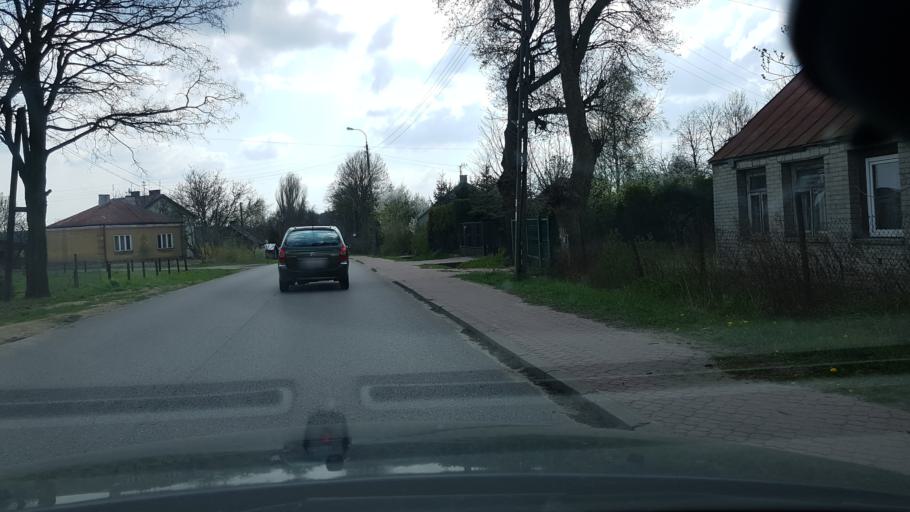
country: PL
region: Masovian Voivodeship
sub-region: Powiat minski
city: Kaluszyn
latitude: 52.2043
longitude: 21.8089
